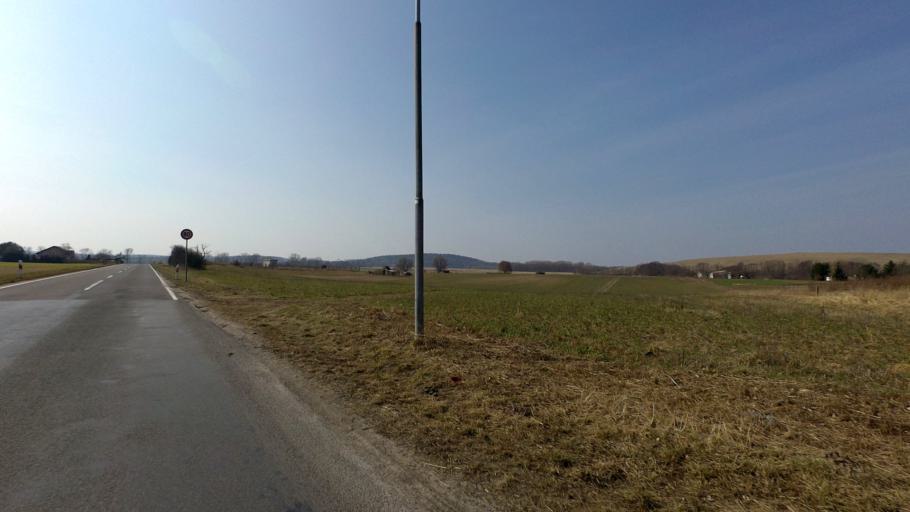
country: DE
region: Brandenburg
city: Ketzin
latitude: 52.4509
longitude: 12.8057
